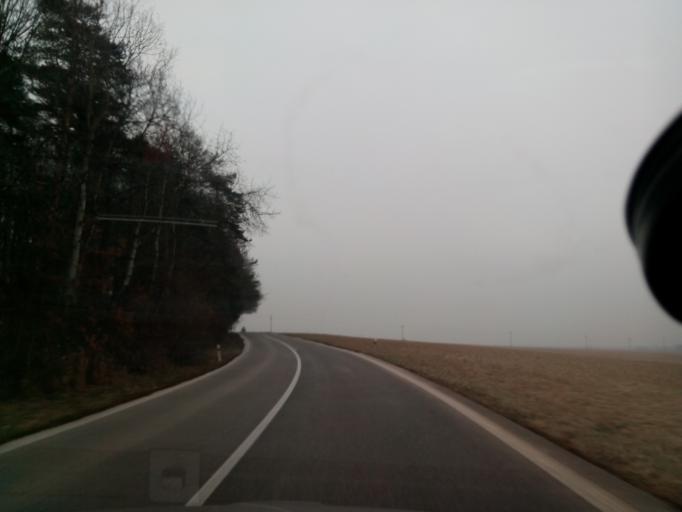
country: SK
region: Kosicky
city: Moldava nad Bodvou
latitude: 48.6786
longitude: 21.0826
